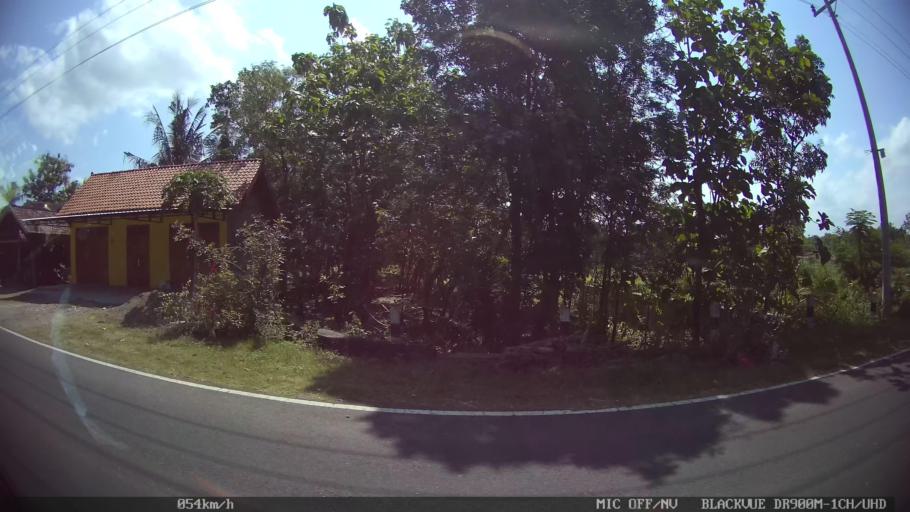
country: ID
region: Daerah Istimewa Yogyakarta
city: Pundong
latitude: -7.9620
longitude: 110.3564
